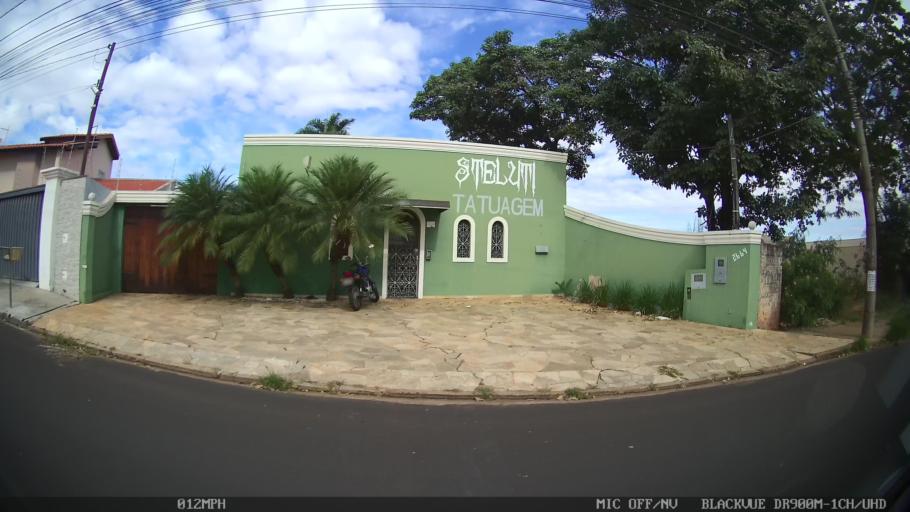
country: BR
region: Sao Paulo
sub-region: Bady Bassitt
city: Bady Bassitt
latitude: -20.8093
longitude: -49.5071
